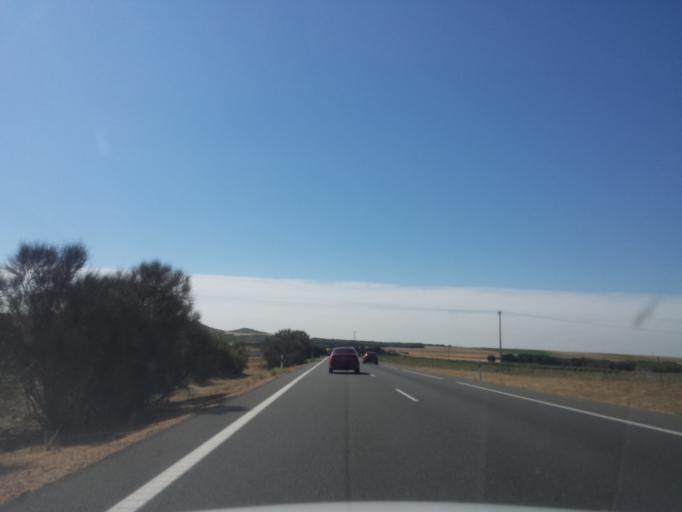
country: ES
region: Castille and Leon
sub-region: Provincia de Valladolid
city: Bercero
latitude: 41.5651
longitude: -5.0883
